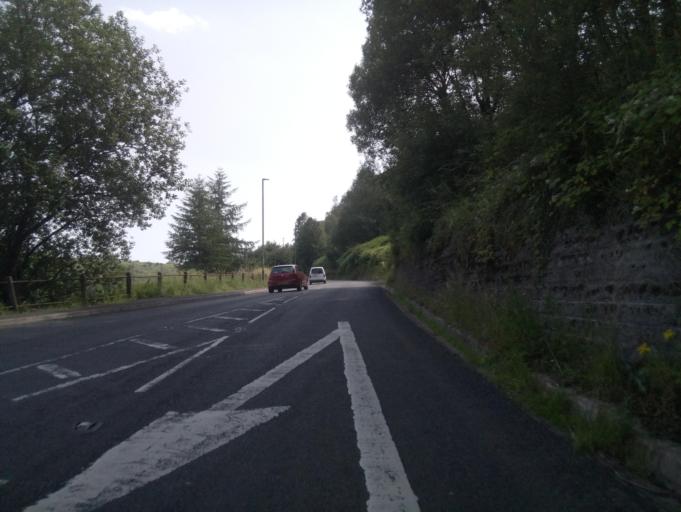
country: GB
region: Wales
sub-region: Caerphilly County Borough
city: New Tredegar
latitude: 51.7076
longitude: -3.2281
